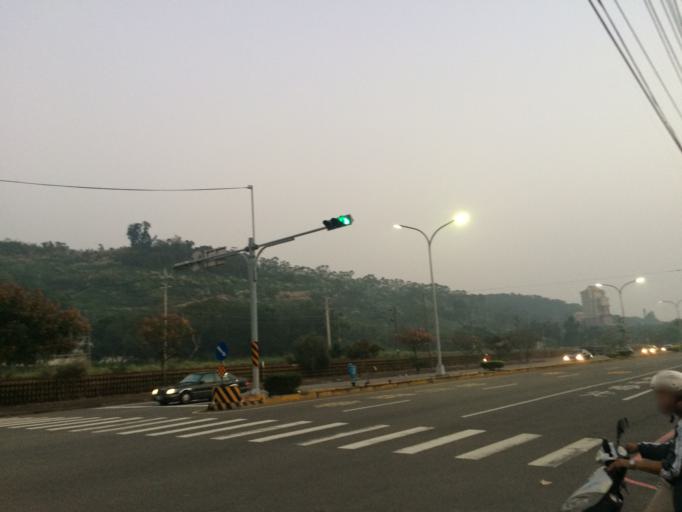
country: TW
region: Taiwan
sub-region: Hsinchu
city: Hsinchu
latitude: 24.7733
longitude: 120.9176
